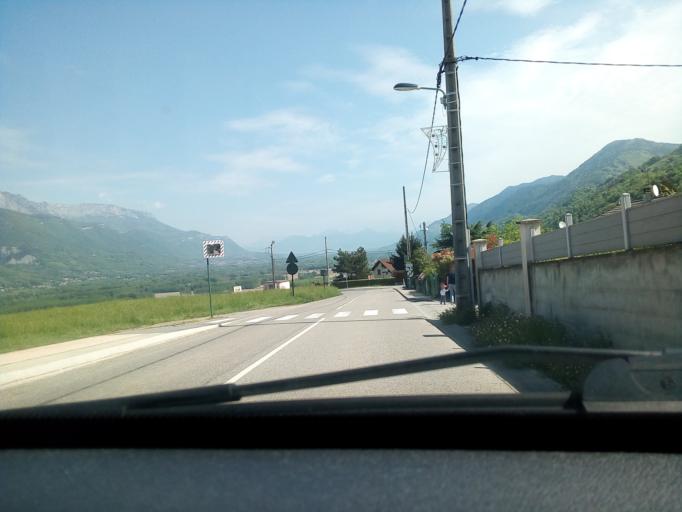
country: FR
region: Rhone-Alpes
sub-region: Departement de l'Isere
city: Le Champ-pres-Froges
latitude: 45.2812
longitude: 5.9387
